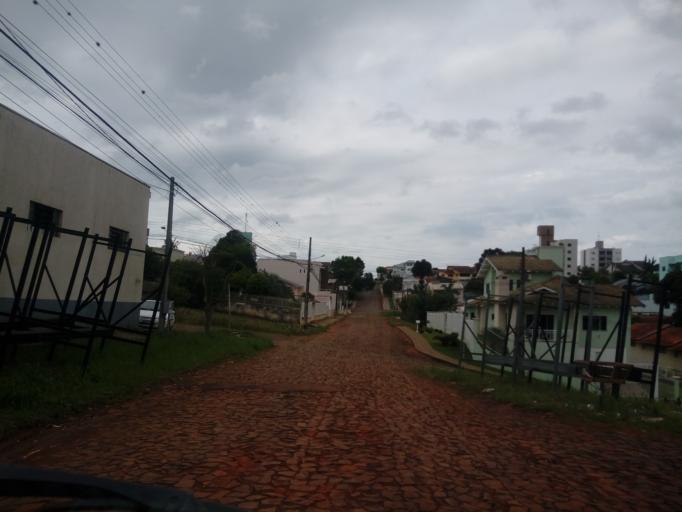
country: BR
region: Santa Catarina
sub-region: Chapeco
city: Chapeco
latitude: -27.0764
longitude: -52.6184
